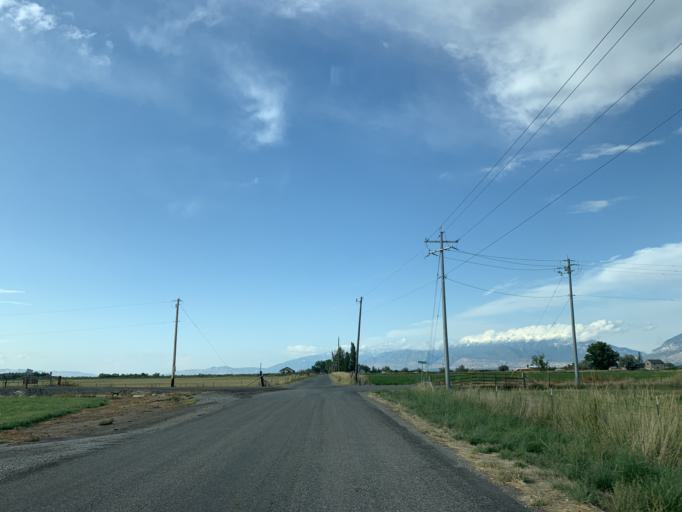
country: US
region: Utah
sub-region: Utah County
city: Benjamin
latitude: 40.1282
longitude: -111.7690
